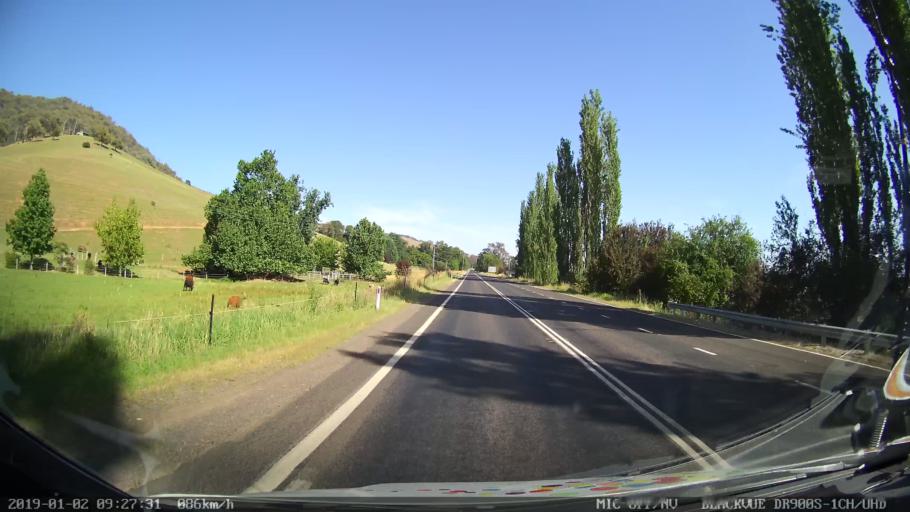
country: AU
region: New South Wales
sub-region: Tumut Shire
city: Tumut
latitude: -35.3610
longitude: 148.2570
